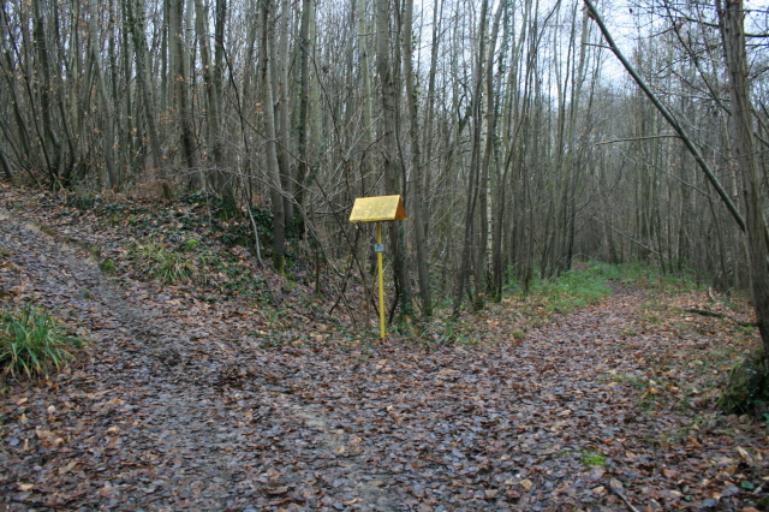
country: FR
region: Ile-de-France
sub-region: Departement des Yvelines
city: Vaux-sur-Seine
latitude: 49.0154
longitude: 1.9800
